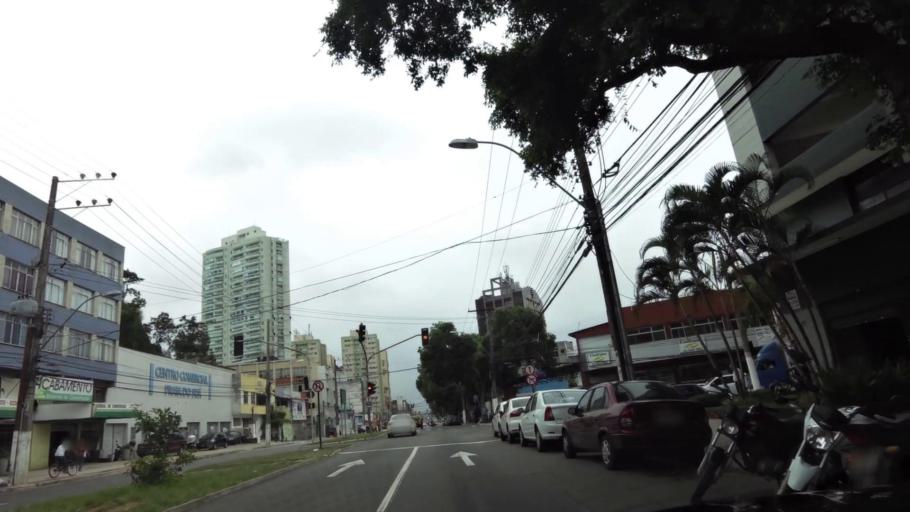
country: BR
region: Espirito Santo
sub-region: Vila Velha
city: Vila Velha
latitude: -20.3139
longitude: -40.3019
